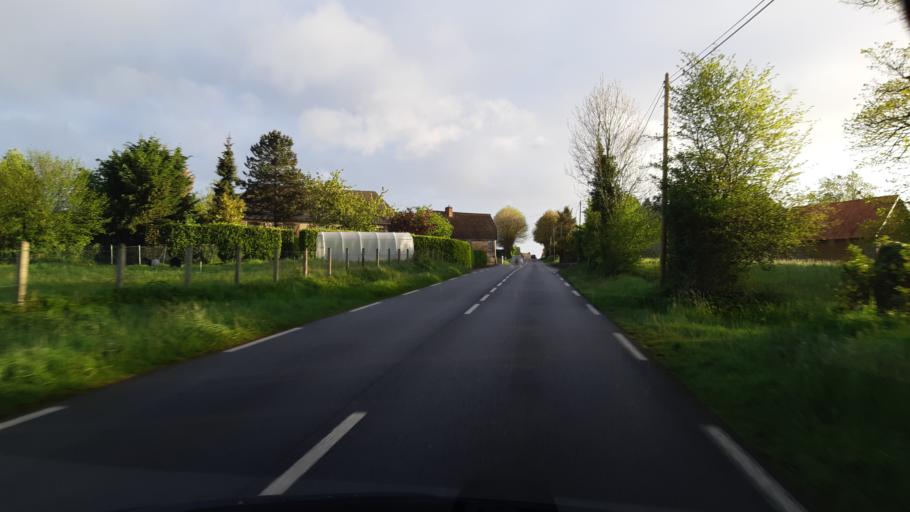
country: FR
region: Lower Normandy
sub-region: Departement de la Manche
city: Tessy-sur-Vire
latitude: 49.0240
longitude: -1.1459
